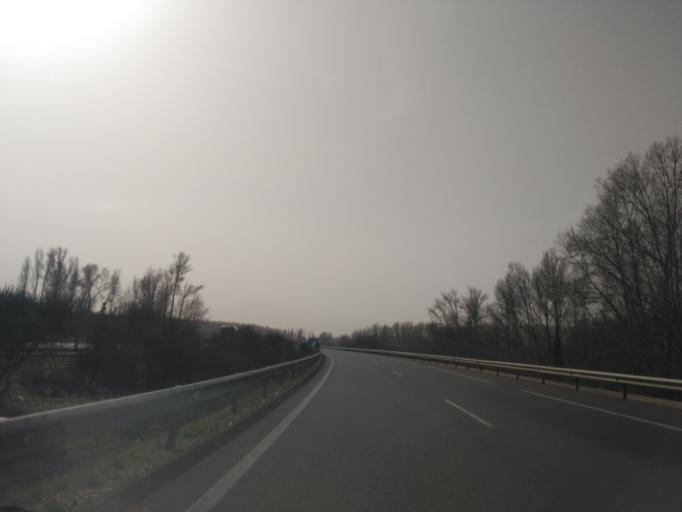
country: ES
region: Castille and Leon
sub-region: Provincia de Palencia
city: Duenas
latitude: 41.8952
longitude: -4.5229
